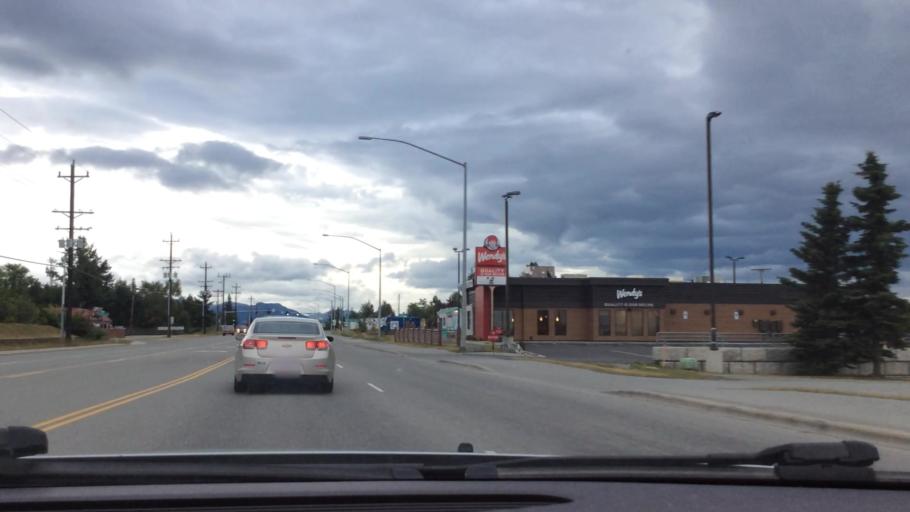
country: US
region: Alaska
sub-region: Anchorage Municipality
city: Anchorage
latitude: 61.1183
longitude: -149.8614
